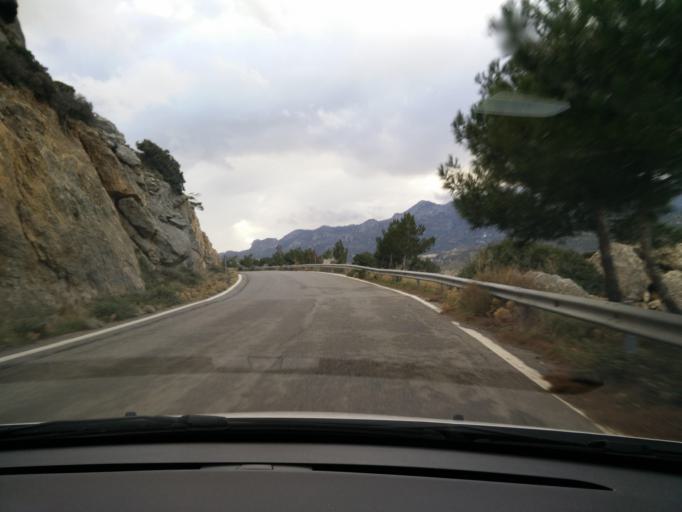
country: GR
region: Crete
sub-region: Nomos Lasithiou
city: Gra Liyia
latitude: 35.0766
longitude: 25.7046
